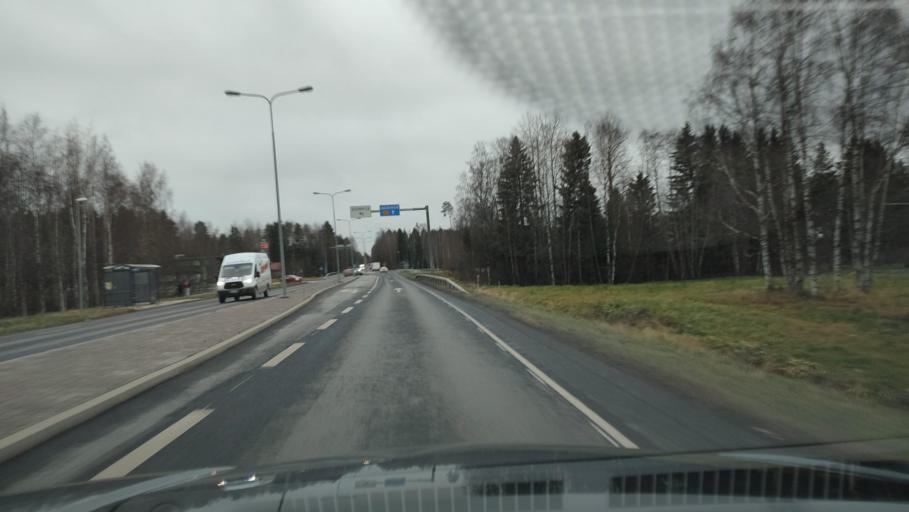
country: FI
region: Southern Ostrobothnia
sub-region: Seinaejoki
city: Ilmajoki
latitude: 62.7714
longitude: 22.6819
